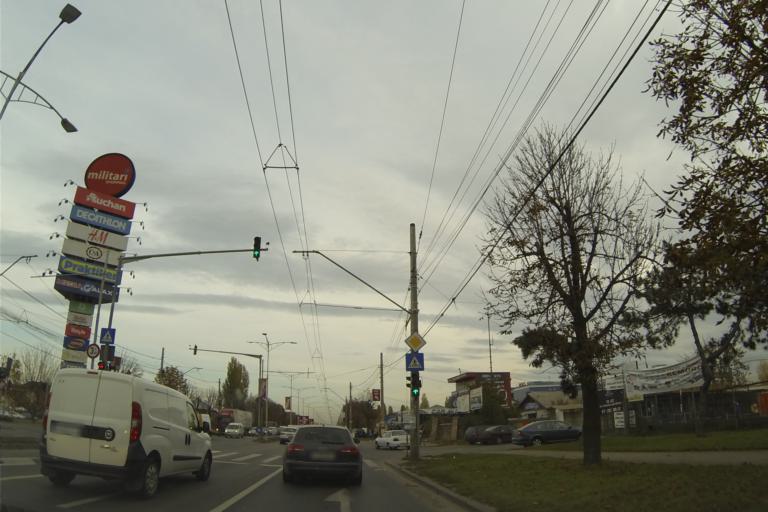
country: RO
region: Ilfov
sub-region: Comuna Chiajna
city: Chiajna
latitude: 44.4349
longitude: 25.9829
